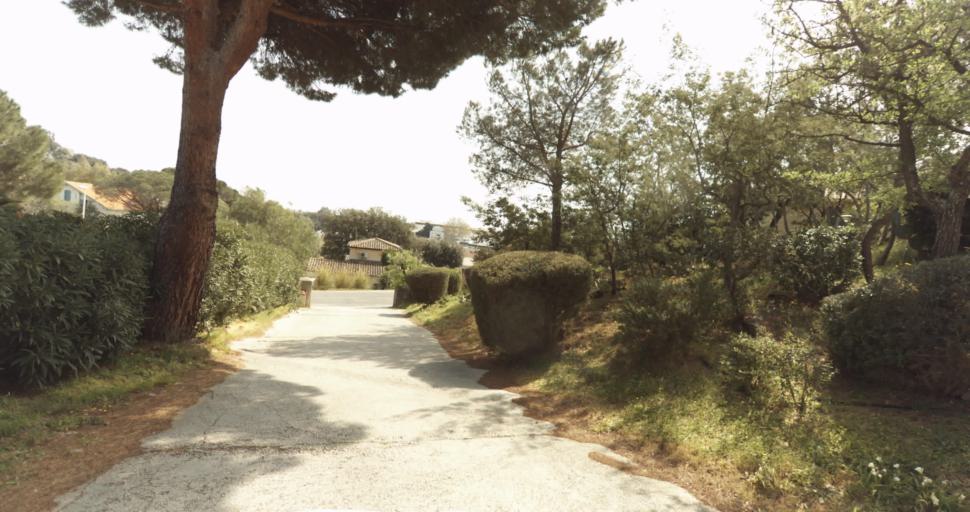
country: FR
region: Provence-Alpes-Cote d'Azur
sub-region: Departement du Var
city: Le Lavandou
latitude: 43.1415
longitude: 6.3545
